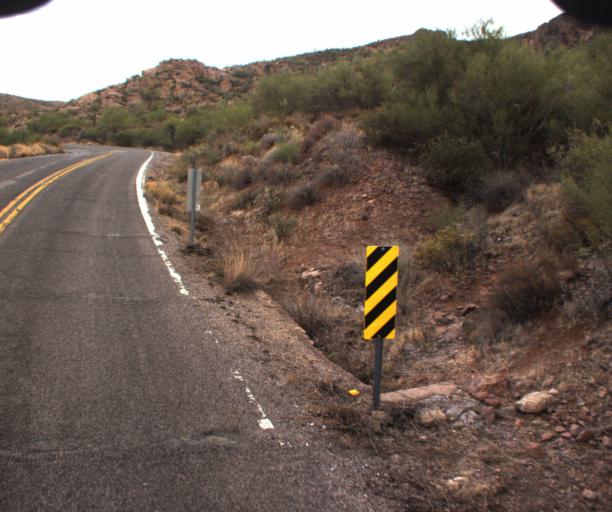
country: US
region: Arizona
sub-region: Pinal County
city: Apache Junction
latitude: 33.5295
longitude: -111.4107
